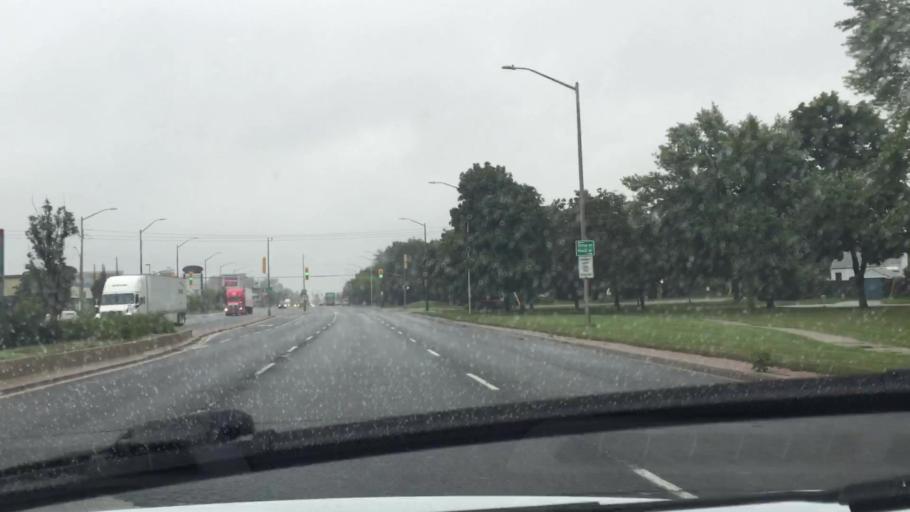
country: CA
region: Ontario
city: Windsor
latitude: 42.2867
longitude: -83.0578
